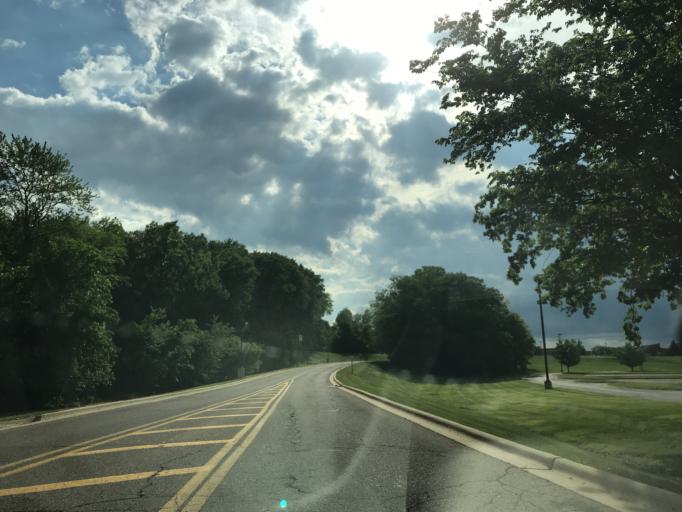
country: US
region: Michigan
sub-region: Oakland County
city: Farmington Hills
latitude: 42.4922
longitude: -83.3635
